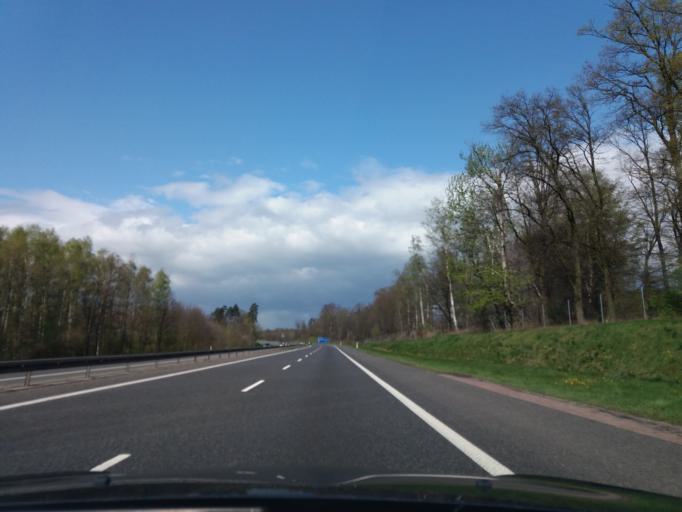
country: PL
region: Opole Voivodeship
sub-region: Powiat strzelecki
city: Ujazd
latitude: 50.4384
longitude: 18.3629
